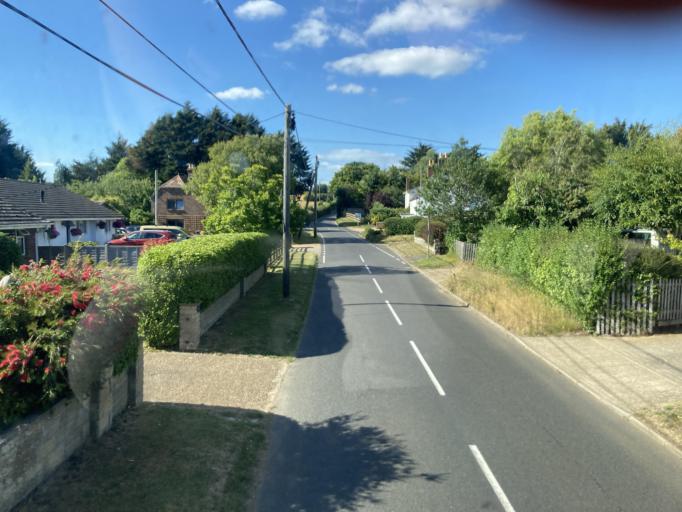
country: GB
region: England
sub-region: Isle of Wight
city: Newchurch
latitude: 50.6623
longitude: -1.2550
